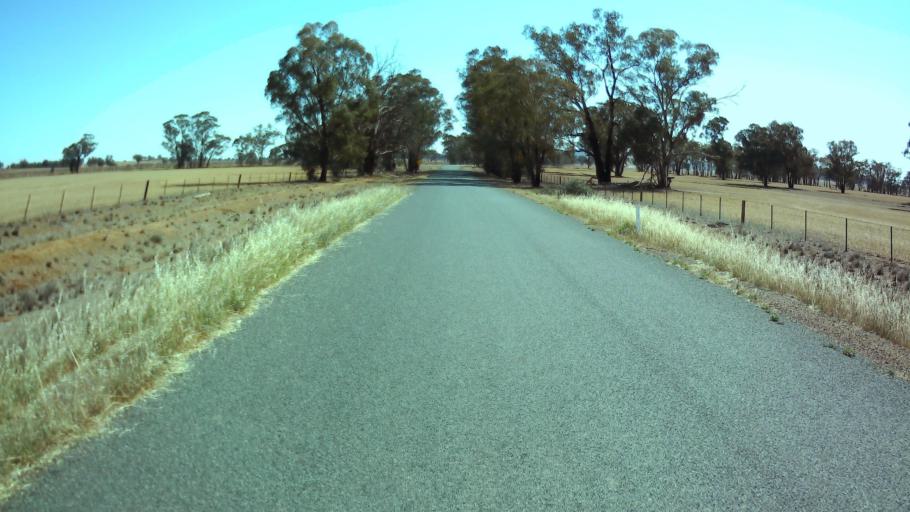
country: AU
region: New South Wales
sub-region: Weddin
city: Grenfell
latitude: -33.7314
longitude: 147.8883
